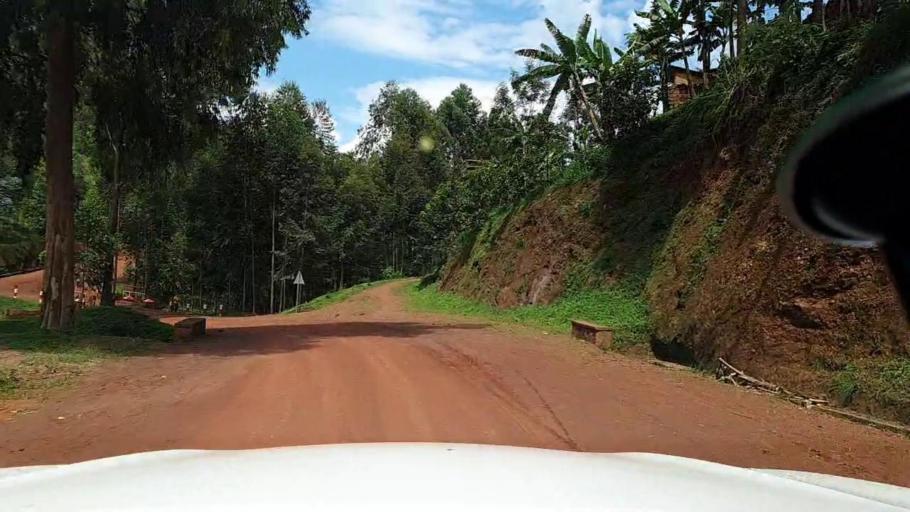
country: RW
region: Northern Province
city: Byumba
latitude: -1.7298
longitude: 29.8563
